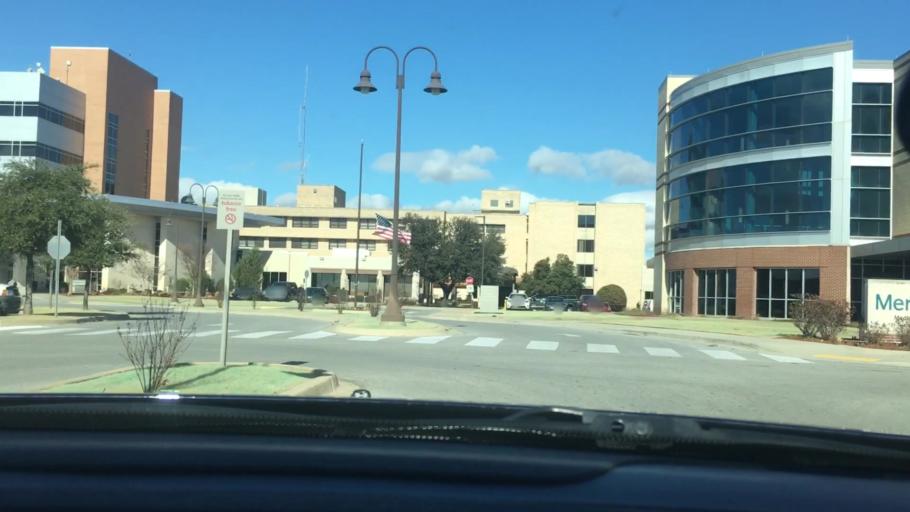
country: US
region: Oklahoma
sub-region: Carter County
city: Ardmore
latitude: 34.1878
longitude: -97.1405
